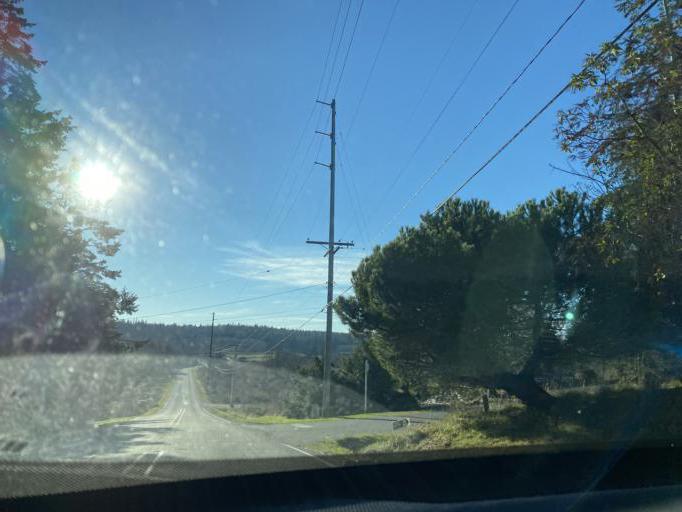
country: US
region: Washington
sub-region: Island County
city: Camano
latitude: 48.1111
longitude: -122.5670
